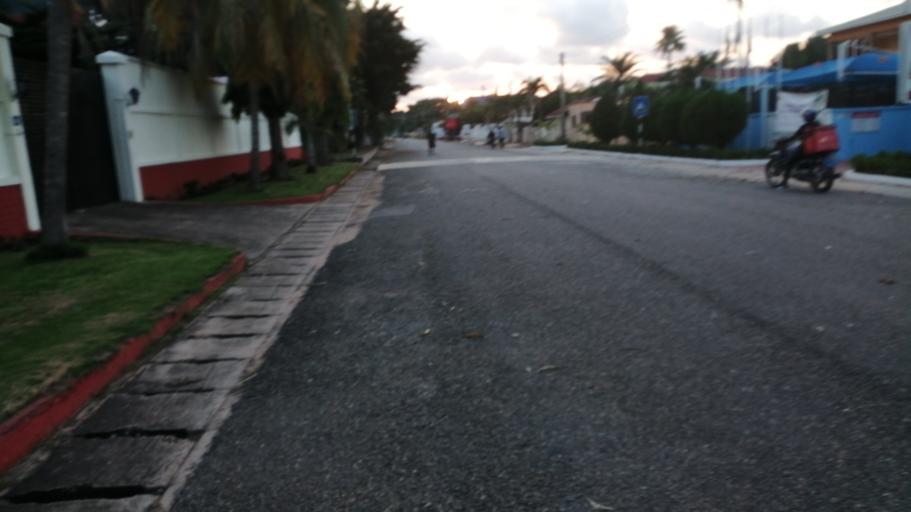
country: GH
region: Greater Accra
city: Medina Estates
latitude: 5.6187
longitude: -0.1807
